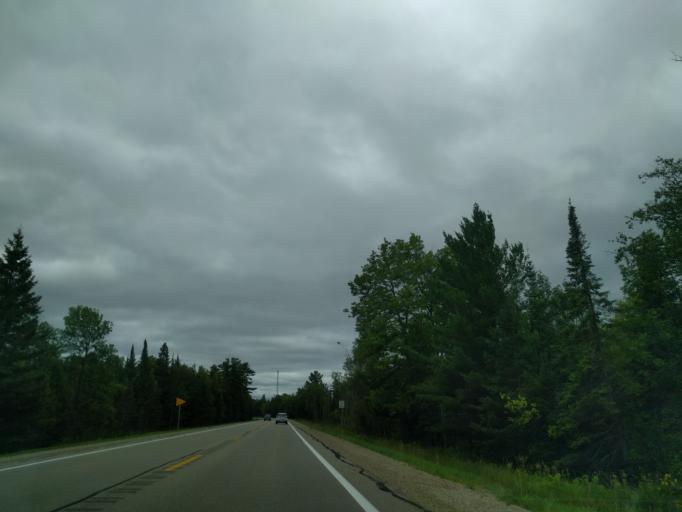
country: US
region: Michigan
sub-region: Delta County
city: Escanaba
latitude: 45.4547
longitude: -87.3345
